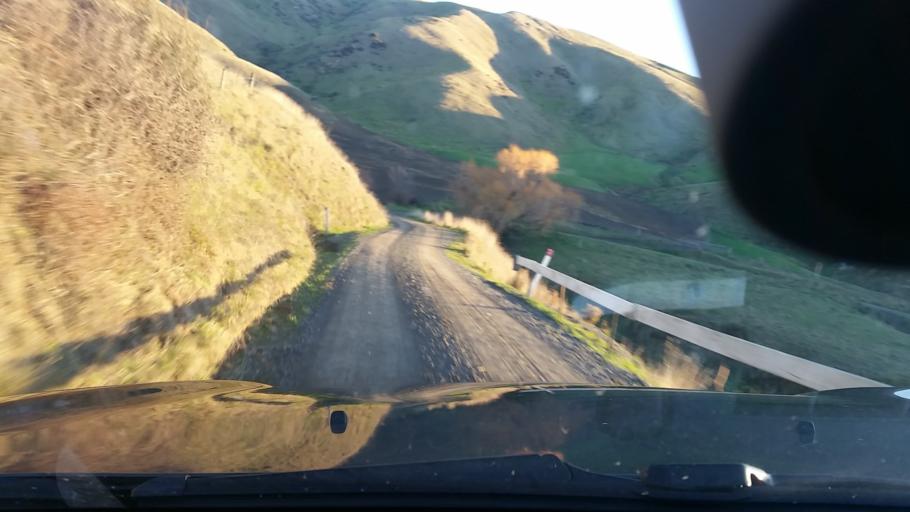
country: NZ
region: Marlborough
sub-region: Marlborough District
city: Blenheim
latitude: -41.7495
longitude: 174.0686
